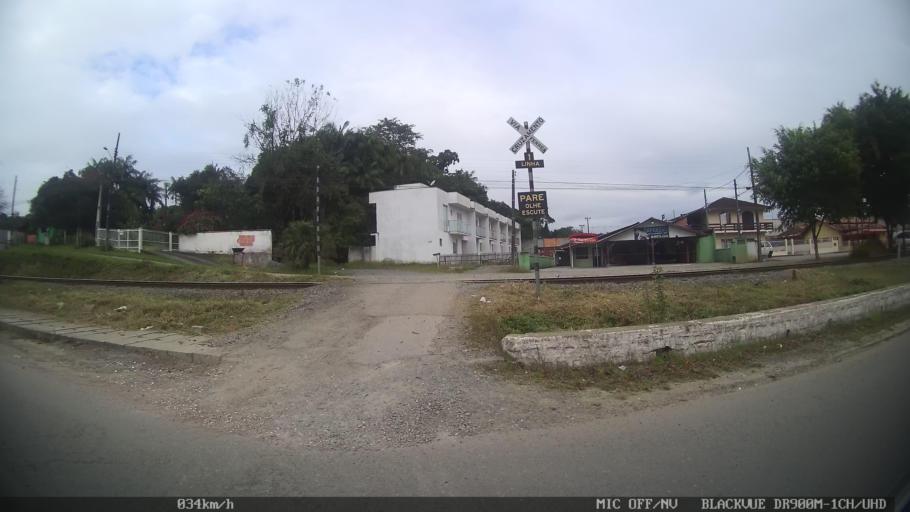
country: BR
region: Santa Catarina
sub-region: Joinville
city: Joinville
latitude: -26.3296
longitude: -48.8655
